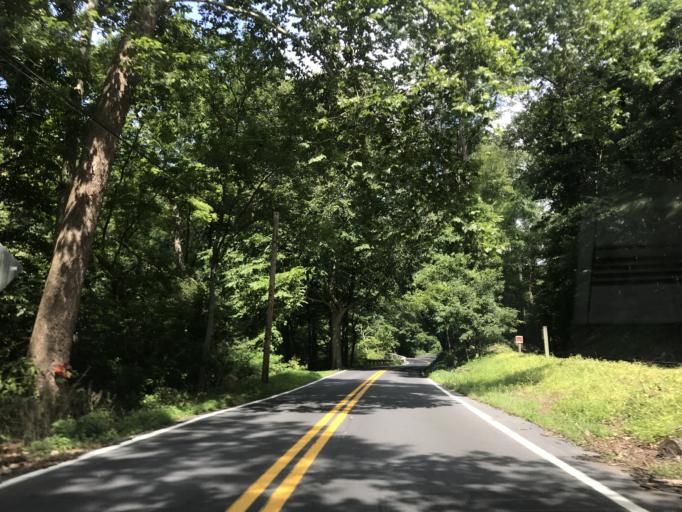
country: US
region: Delaware
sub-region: New Castle County
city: Hockessin
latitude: 39.8014
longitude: -75.6536
